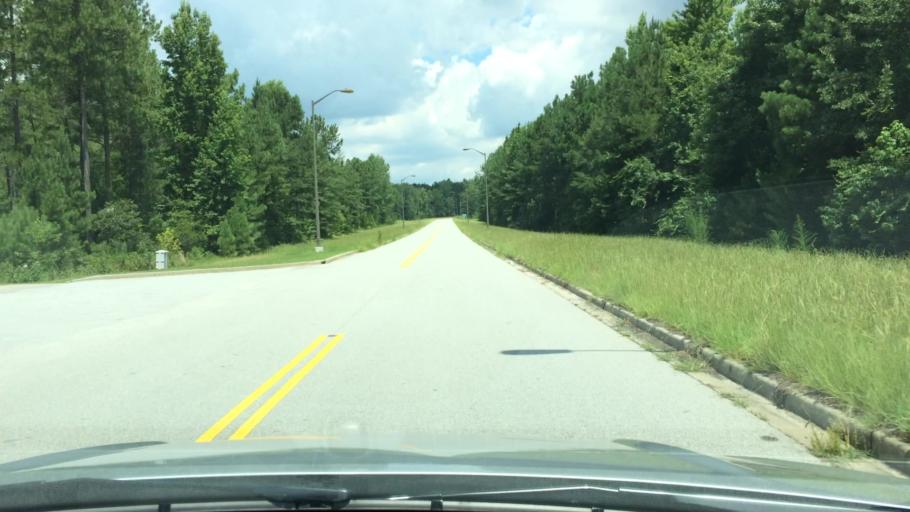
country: US
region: South Carolina
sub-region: Calhoun County
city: Oak Grove
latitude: 33.7978
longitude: -81.0035
